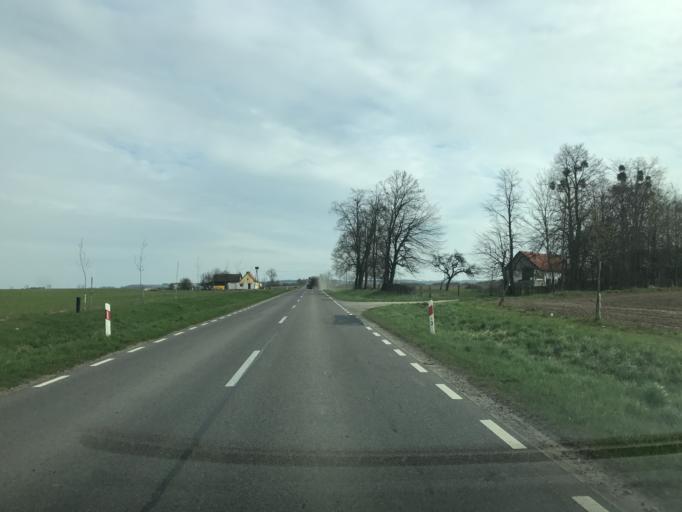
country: PL
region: Warmian-Masurian Voivodeship
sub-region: Powiat ostrodzki
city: Gierzwald
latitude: 53.5118
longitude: 20.0854
